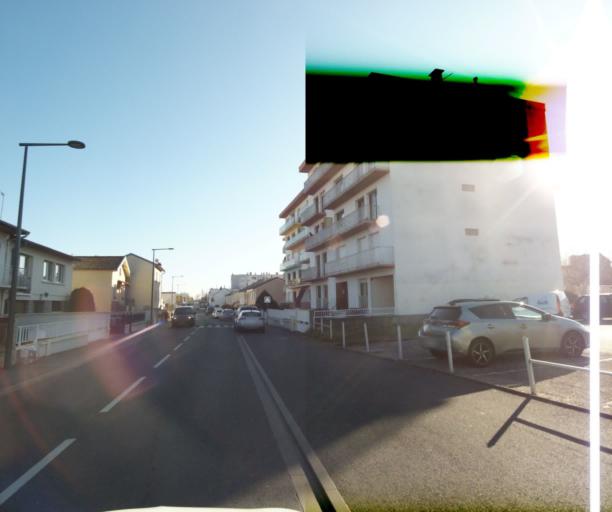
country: FR
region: Lorraine
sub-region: Departement de Meurthe-et-Moselle
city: Saint-Max
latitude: 48.7012
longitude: 6.2143
